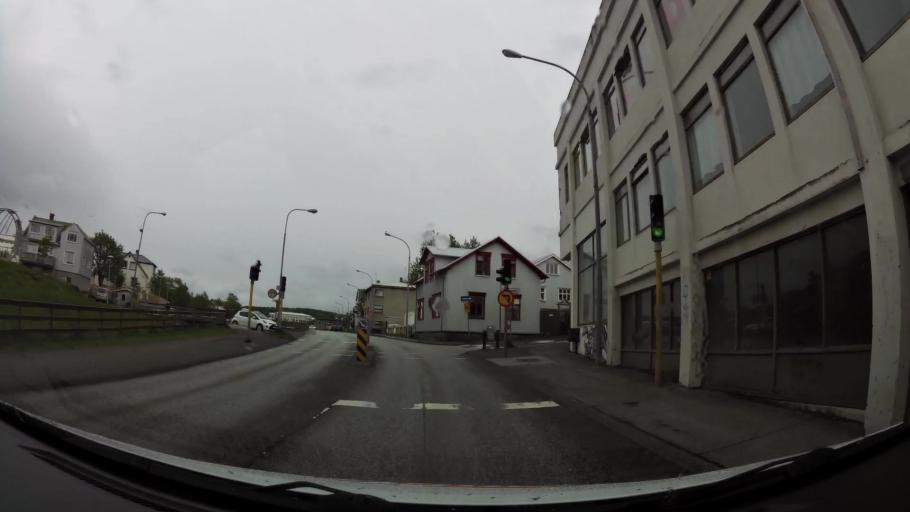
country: IS
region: Capital Region
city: Hafnarfjoerdur
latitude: 64.0668
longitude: -21.9524
